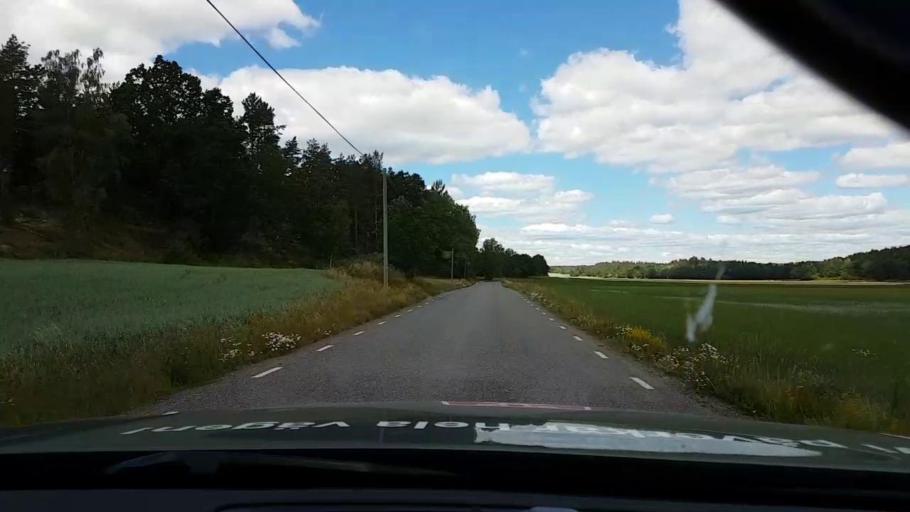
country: SE
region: Kalmar
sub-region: Vasterviks Kommun
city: Forserum
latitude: 57.9955
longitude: 16.5985
